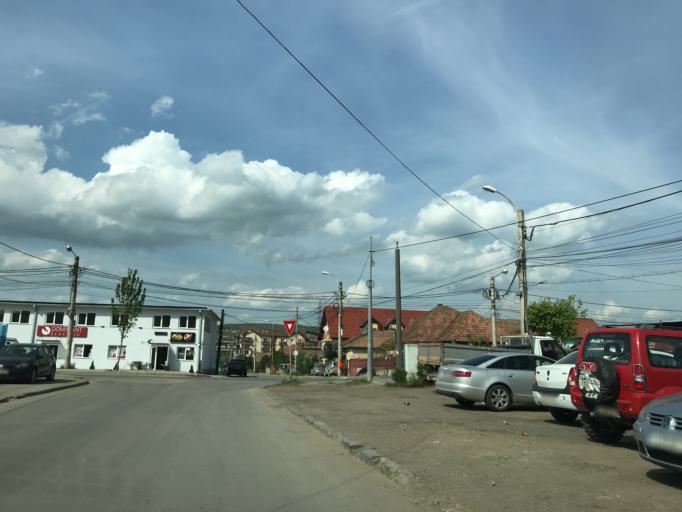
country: RO
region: Cluj
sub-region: Municipiul Cluj-Napoca
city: Cluj-Napoca
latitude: 46.7865
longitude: 23.6392
